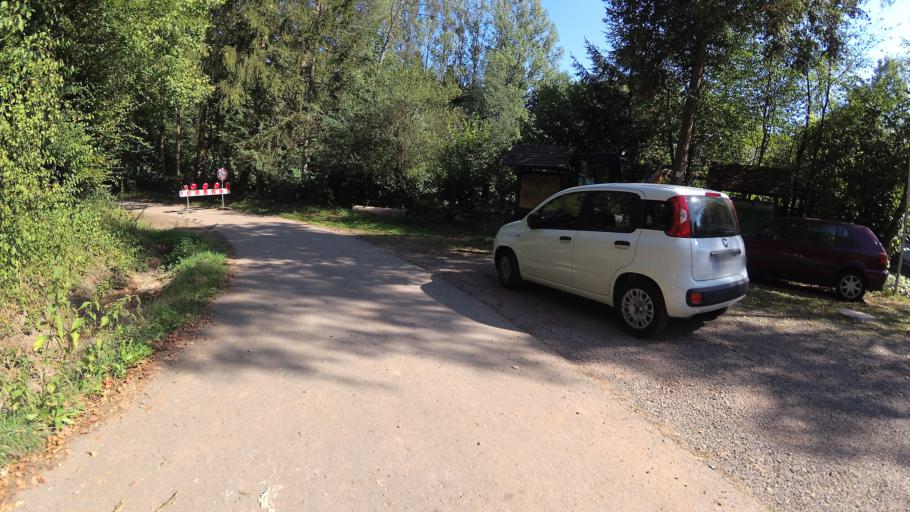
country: DE
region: Saarland
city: Eppelborn
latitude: 49.3839
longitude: 6.9633
